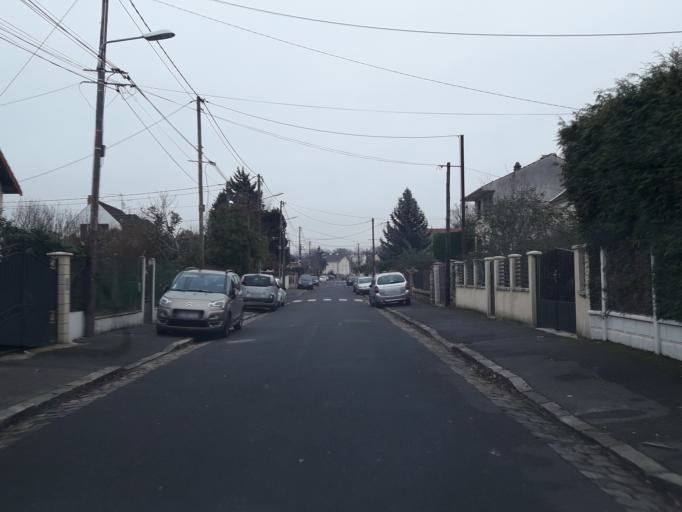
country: FR
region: Ile-de-France
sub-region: Departement de l'Essonne
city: Sainte-Genevieve-des-Bois
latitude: 48.6424
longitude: 2.3361
